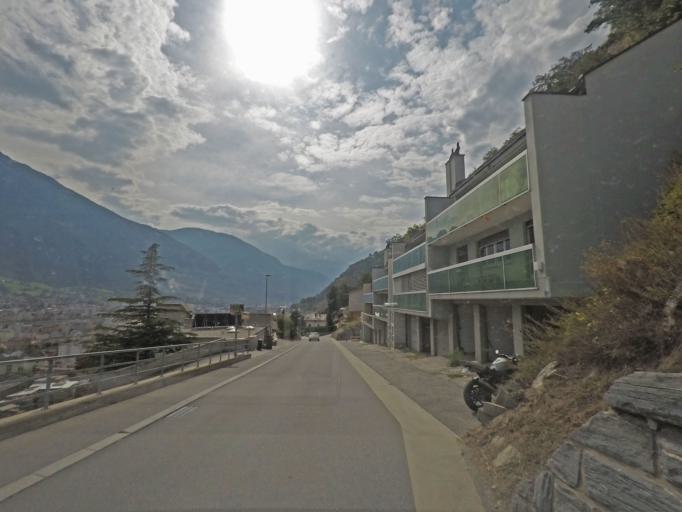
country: CH
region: Valais
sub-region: Brig District
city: Naters
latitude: 46.3293
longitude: 7.9963
